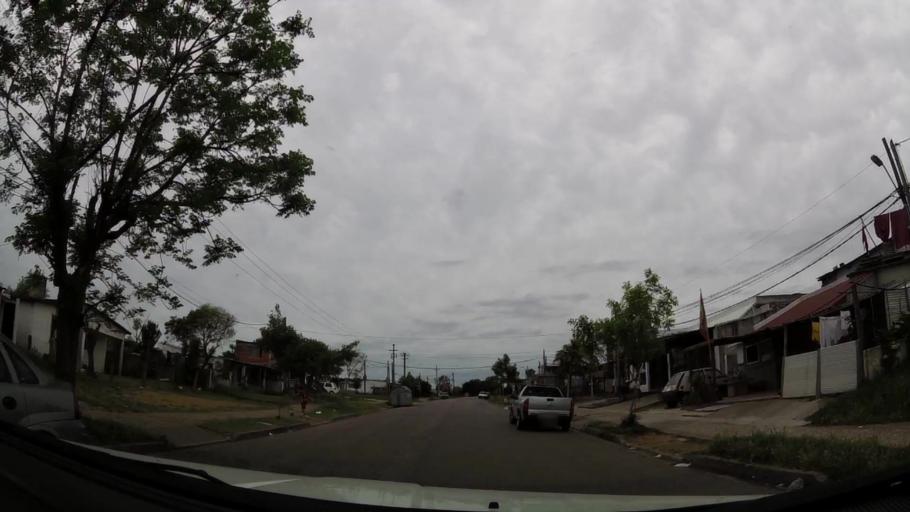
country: UY
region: Maldonado
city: Maldonado
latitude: -34.8923
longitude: -54.9402
